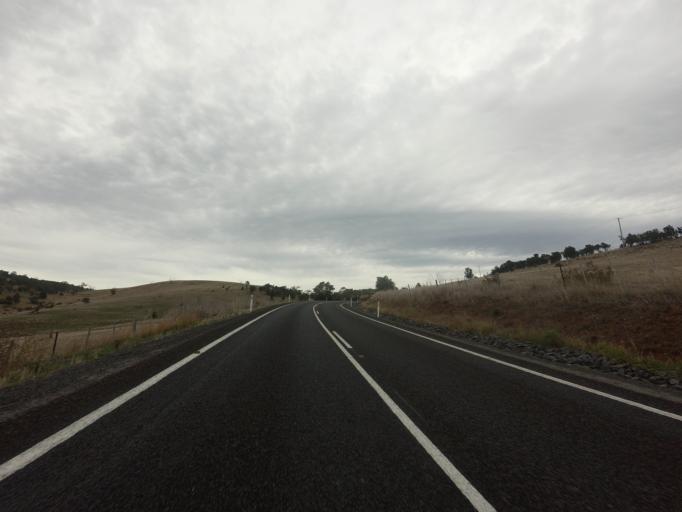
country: AU
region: Tasmania
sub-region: Derwent Valley
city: New Norfolk
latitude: -42.5582
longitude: 146.8706
